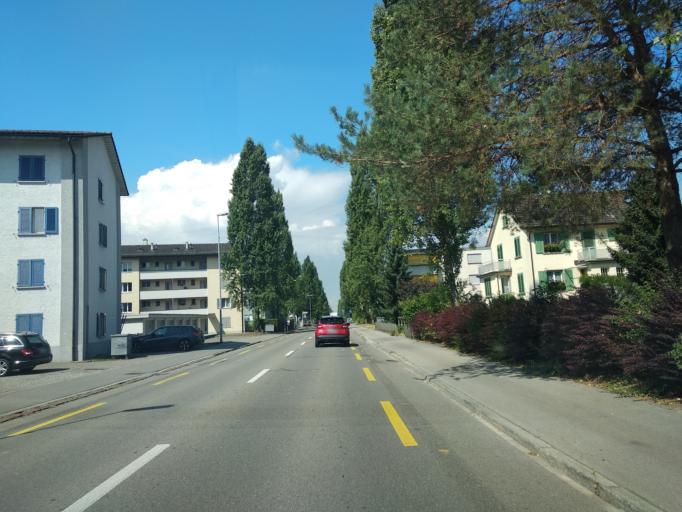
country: CH
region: Thurgau
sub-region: Frauenfeld District
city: Frauenfeld
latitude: 47.5617
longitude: 8.8857
